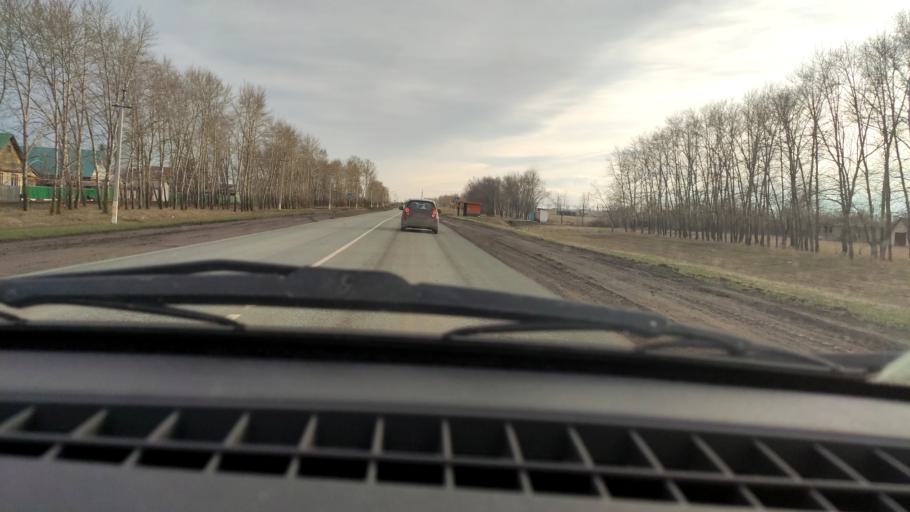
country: RU
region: Bashkortostan
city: Davlekanovo
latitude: 54.3917
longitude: 55.2038
